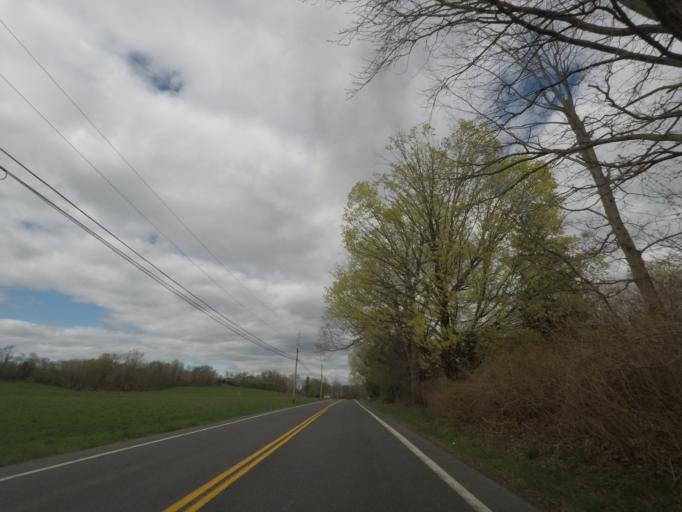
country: US
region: New York
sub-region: Columbia County
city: Philmont
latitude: 42.2955
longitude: -73.6411
